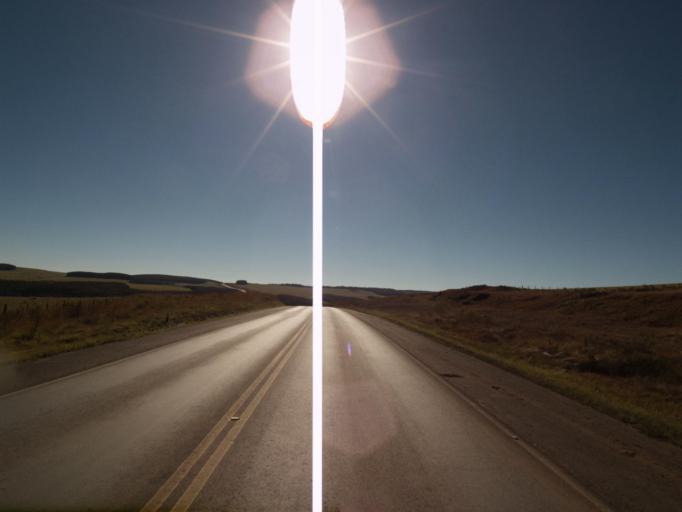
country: BR
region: Parana
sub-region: Palmas
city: Palmas
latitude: -26.7656
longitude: -51.6699
